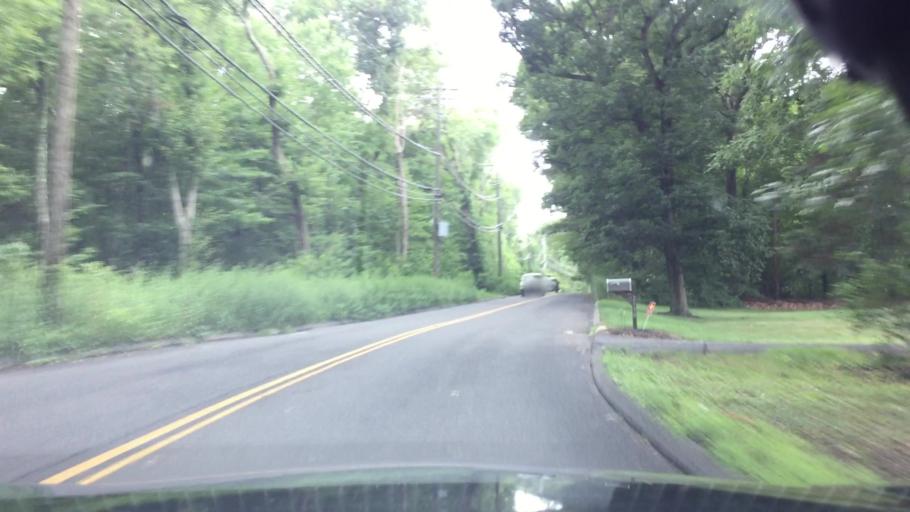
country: US
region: Connecticut
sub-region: Fairfield County
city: Shelton
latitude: 41.2632
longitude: -73.1200
